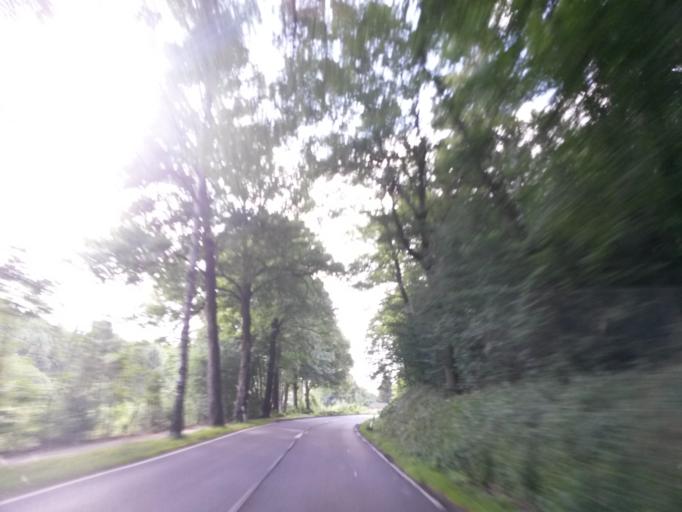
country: DE
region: North Rhine-Westphalia
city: Waldbrol
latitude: 50.8952
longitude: 7.6308
